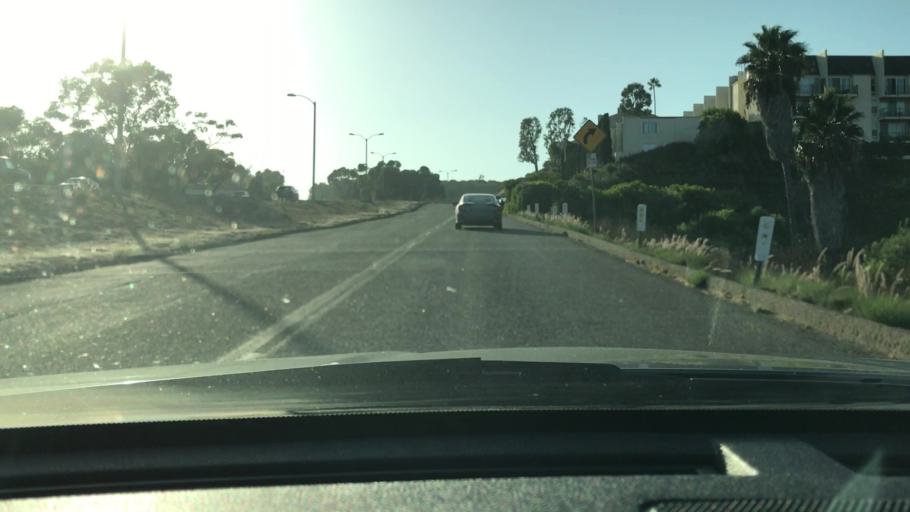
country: US
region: California
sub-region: Los Angeles County
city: Malibu Beach
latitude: 34.0353
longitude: -118.6943
